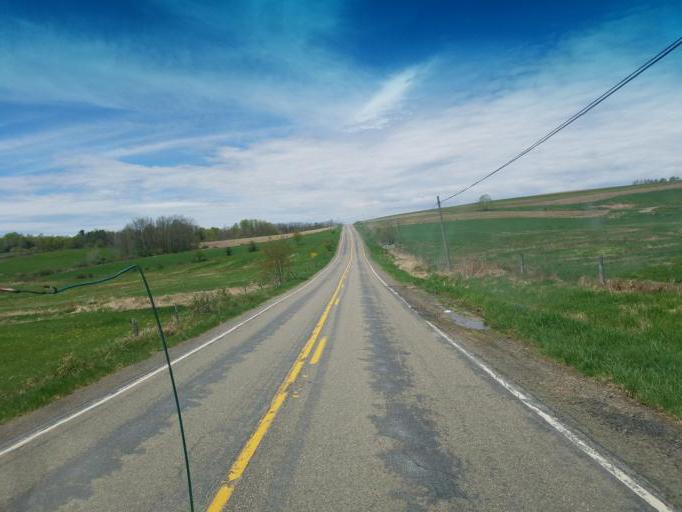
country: US
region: Pennsylvania
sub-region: Tioga County
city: Wellsboro
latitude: 41.7050
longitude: -77.4021
